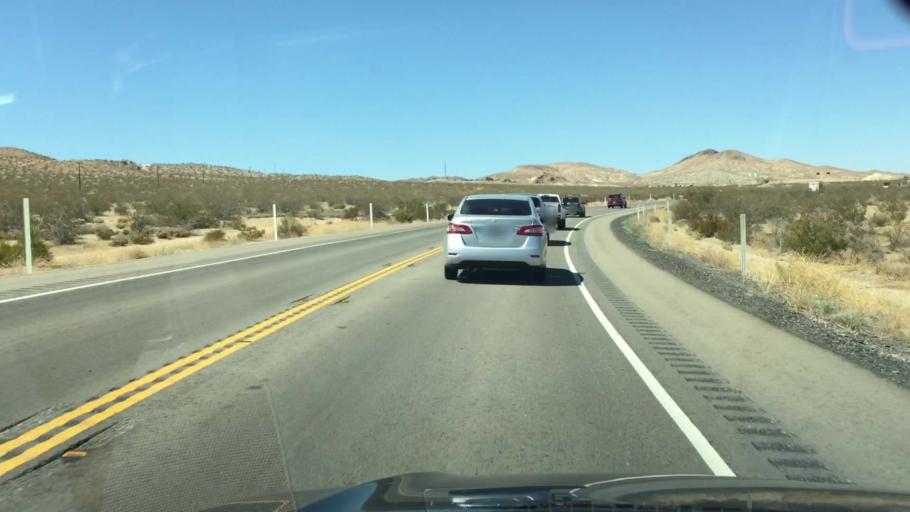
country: US
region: California
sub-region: Kern County
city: Ridgecrest
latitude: 35.3306
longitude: -117.6184
